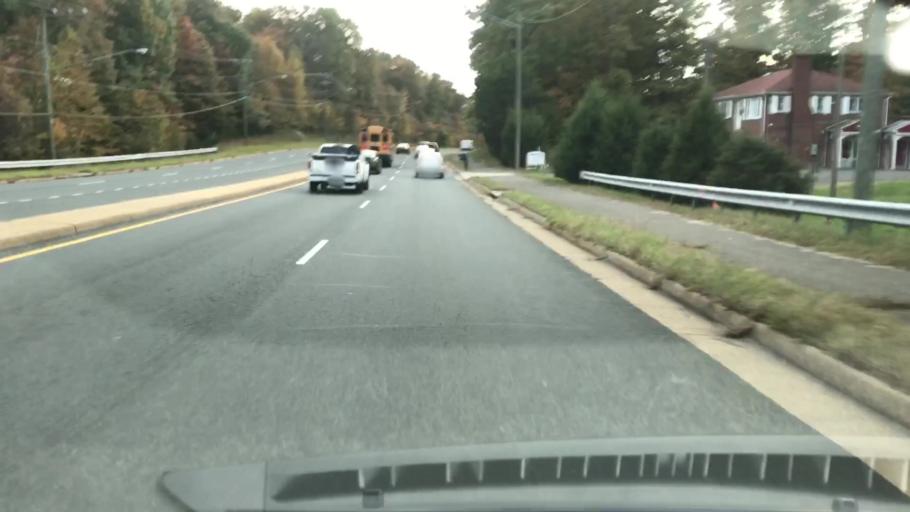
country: US
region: Virginia
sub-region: City of Fairfax
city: Fairfax
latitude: 38.8425
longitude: -77.3414
